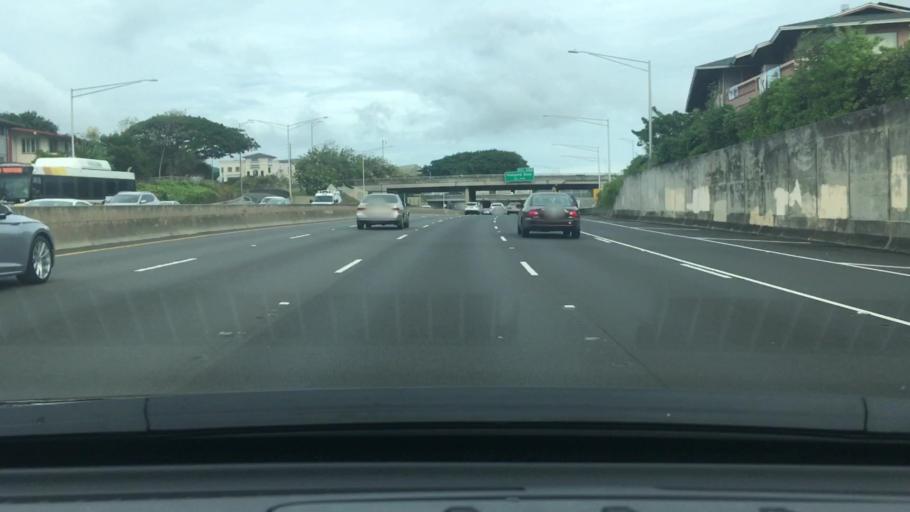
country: US
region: Hawaii
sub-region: Honolulu County
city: Honolulu
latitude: 21.3344
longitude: -157.8753
